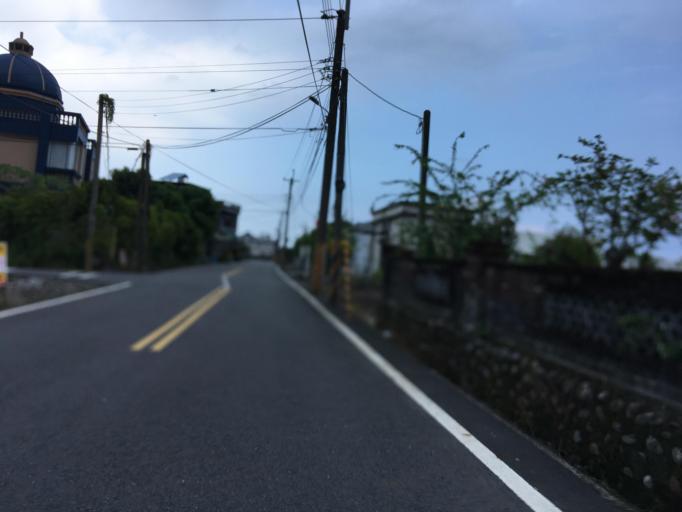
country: TW
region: Taiwan
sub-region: Yilan
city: Yilan
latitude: 24.6838
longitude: 121.7030
